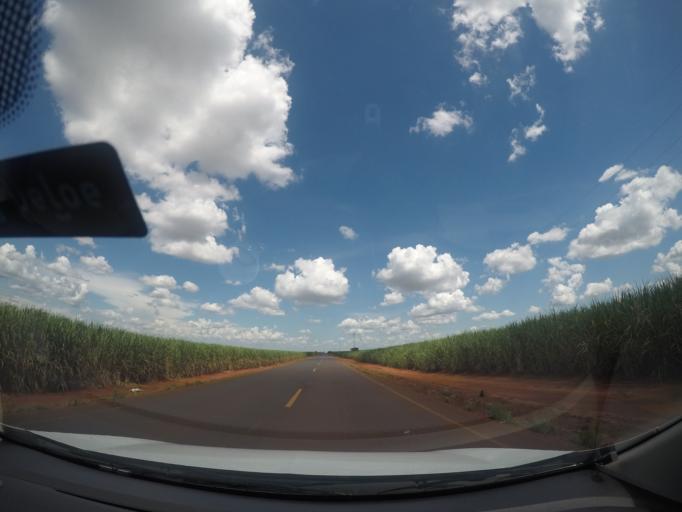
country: BR
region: Minas Gerais
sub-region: Frutal
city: Frutal
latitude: -19.8535
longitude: -48.7350
